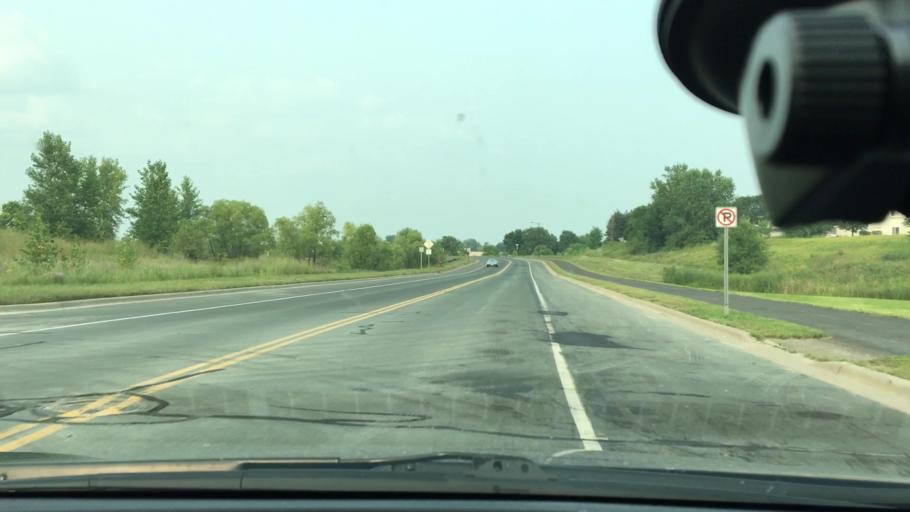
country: US
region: Minnesota
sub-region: Wright County
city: Otsego
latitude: 45.2547
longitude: -93.5634
